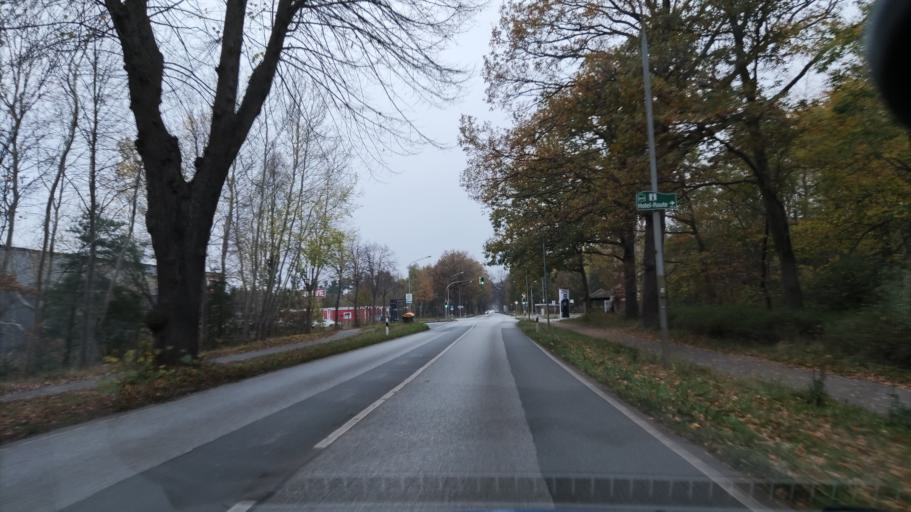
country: DE
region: Schleswig-Holstein
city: Gross Gronau
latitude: 53.8239
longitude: 10.7219
